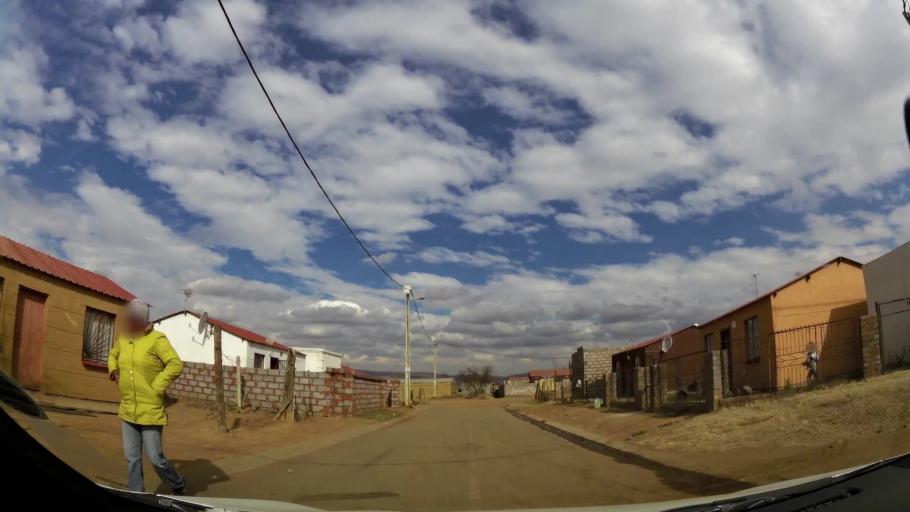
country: ZA
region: Gauteng
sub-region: Ekurhuleni Metropolitan Municipality
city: Germiston
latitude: -26.4130
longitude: 28.1648
